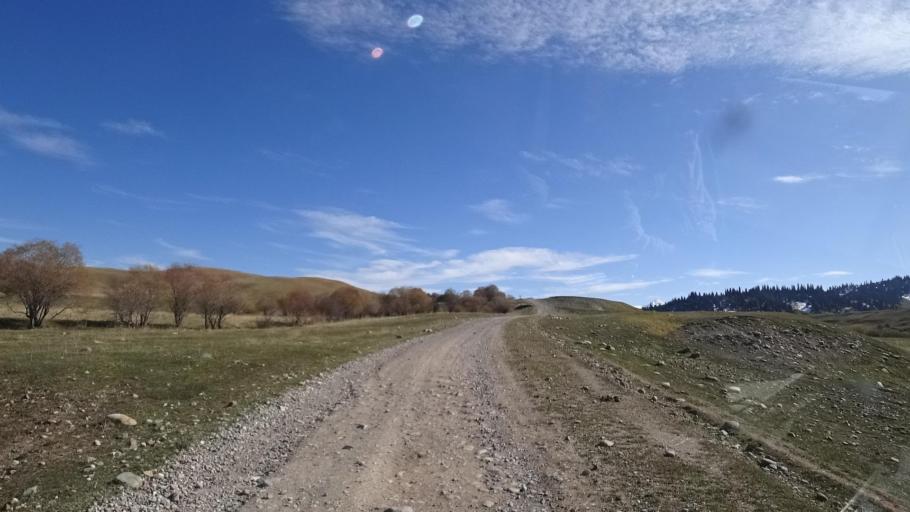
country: KZ
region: Almaty Oblysy
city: Kegen
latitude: 42.7371
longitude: 79.0137
